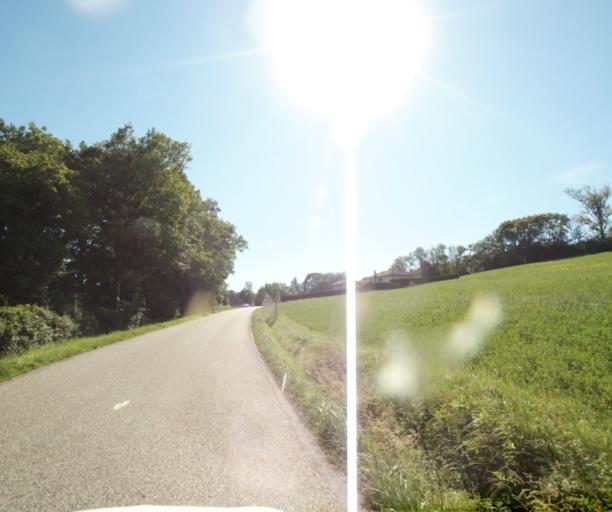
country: FR
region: Rhone-Alpes
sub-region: Departement de la Haute-Savoie
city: Sciez
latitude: 46.2997
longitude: 6.3755
